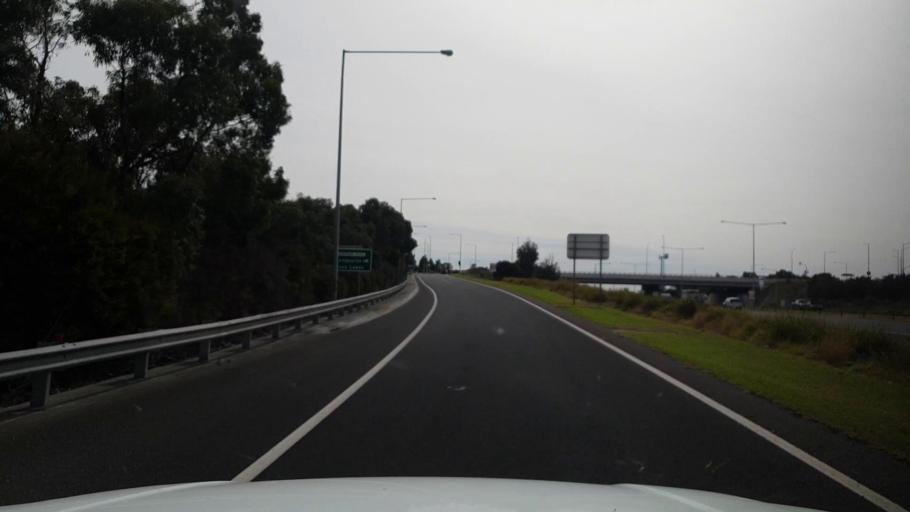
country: AU
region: Victoria
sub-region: Frankston
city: Sandhurst
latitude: -38.0727
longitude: 145.1811
